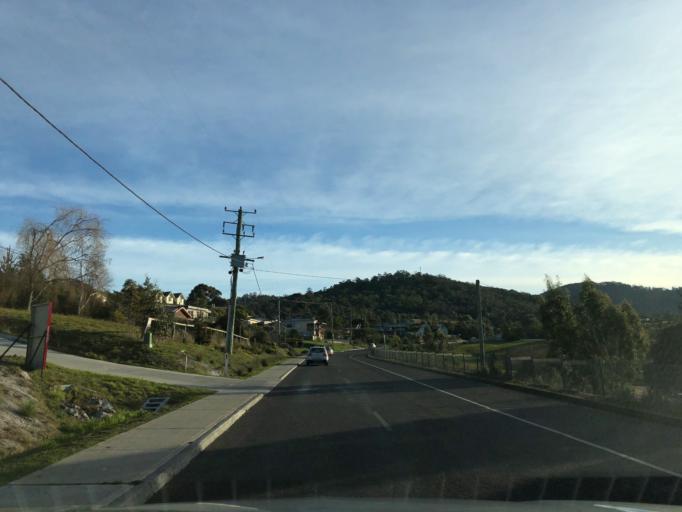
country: AU
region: Tasmania
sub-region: Kingborough
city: Kettering
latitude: -43.1284
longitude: 147.2506
